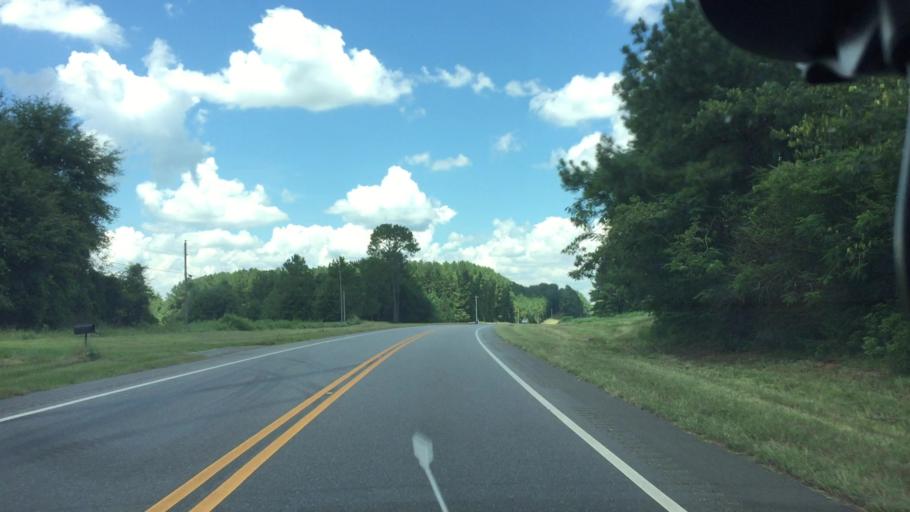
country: US
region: Alabama
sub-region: Pike County
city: Brundidge
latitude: 31.5982
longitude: -85.9467
